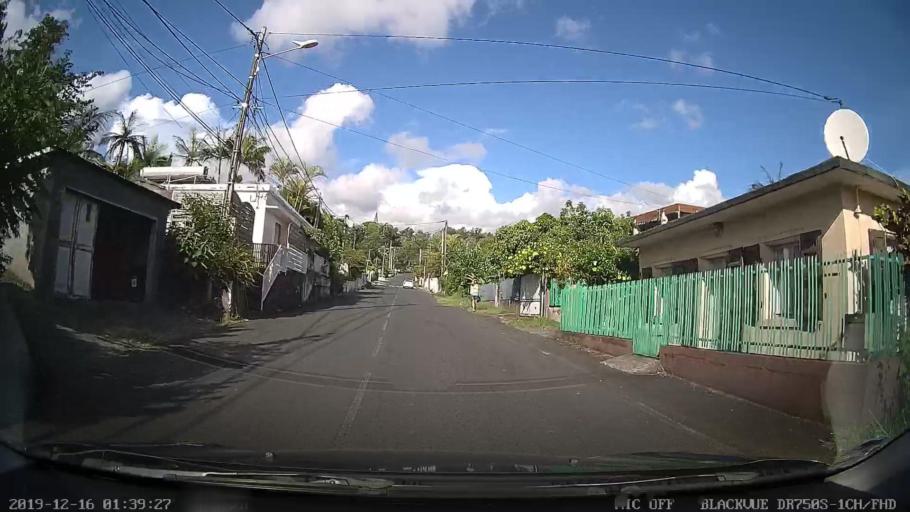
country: RE
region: Reunion
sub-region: Reunion
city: Le Tampon
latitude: -21.2623
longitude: 55.5073
